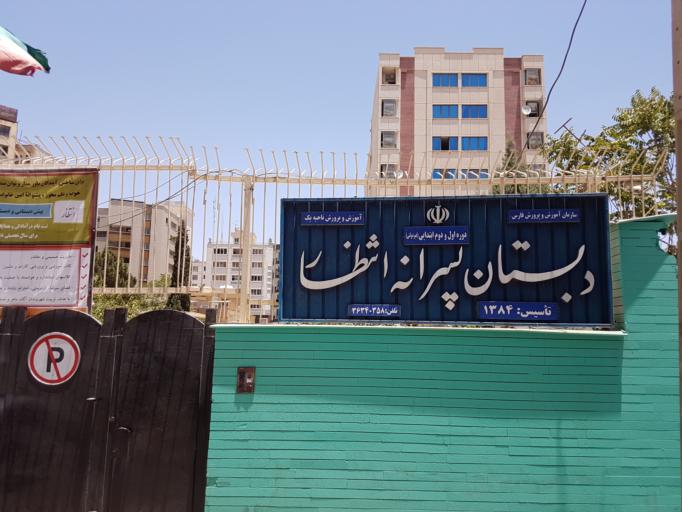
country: IR
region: Fars
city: Shiraz
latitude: 29.6788
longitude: 52.4583
